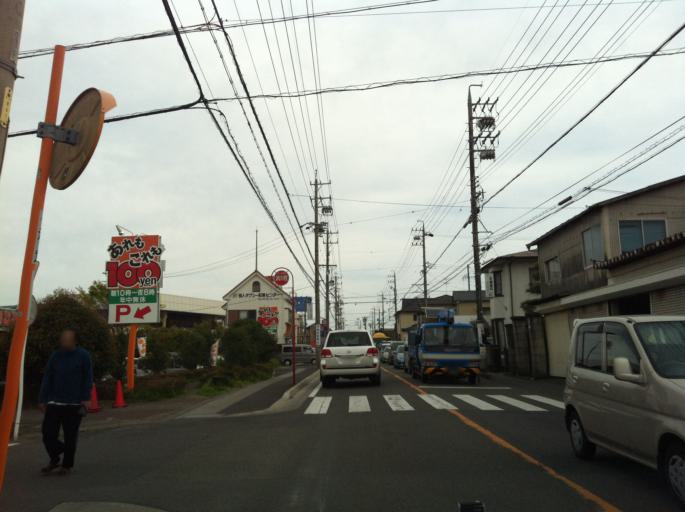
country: JP
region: Shizuoka
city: Shizuoka-shi
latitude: 35.0016
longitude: 138.4697
